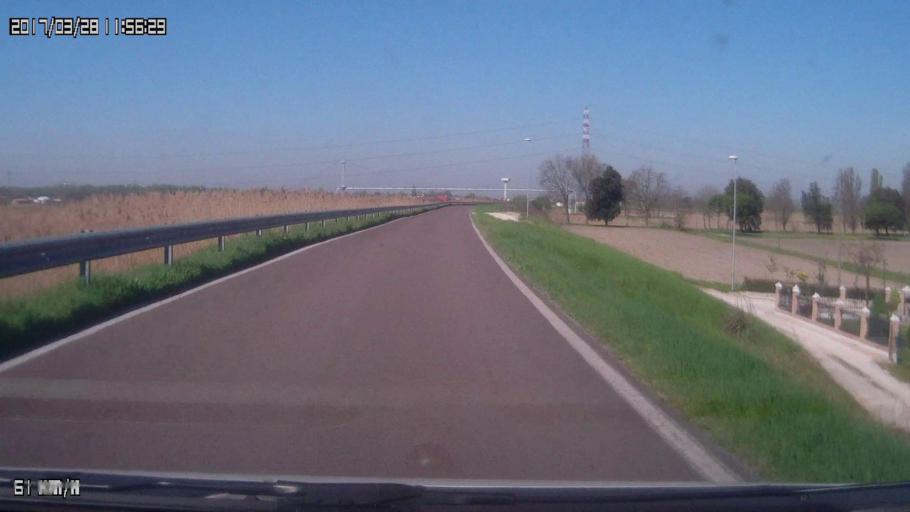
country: IT
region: Veneto
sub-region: Provincia di Venezia
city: Boscochiaro
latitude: 45.1332
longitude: 12.1379
